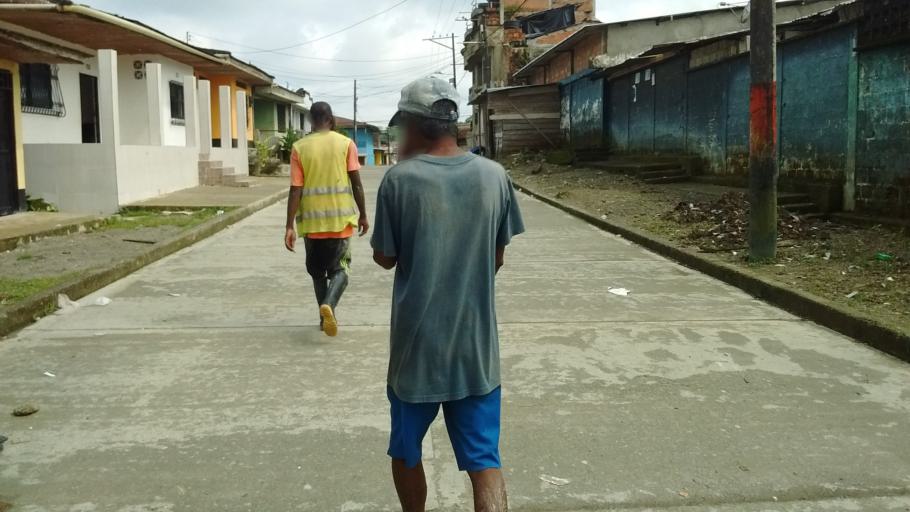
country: CO
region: Cauca
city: Guapi
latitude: 2.5700
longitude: -77.8842
